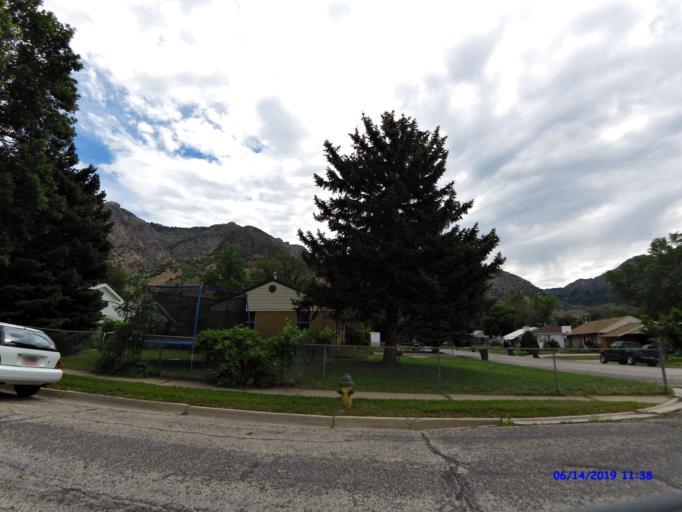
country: US
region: Utah
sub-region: Weber County
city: Ogden
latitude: 41.2499
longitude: -111.9422
